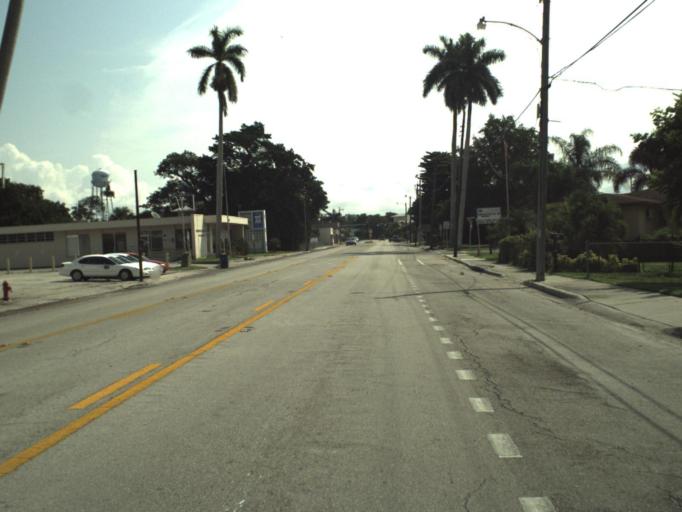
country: US
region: Florida
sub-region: Palm Beach County
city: Pahokee
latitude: 26.8218
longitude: -80.6688
